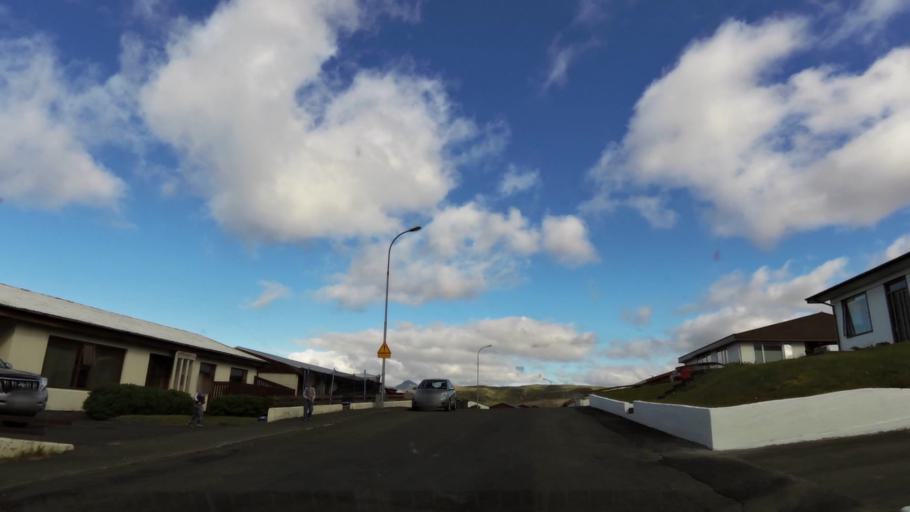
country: IS
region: West
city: Olafsvik
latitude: 64.8908
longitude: -23.7077
